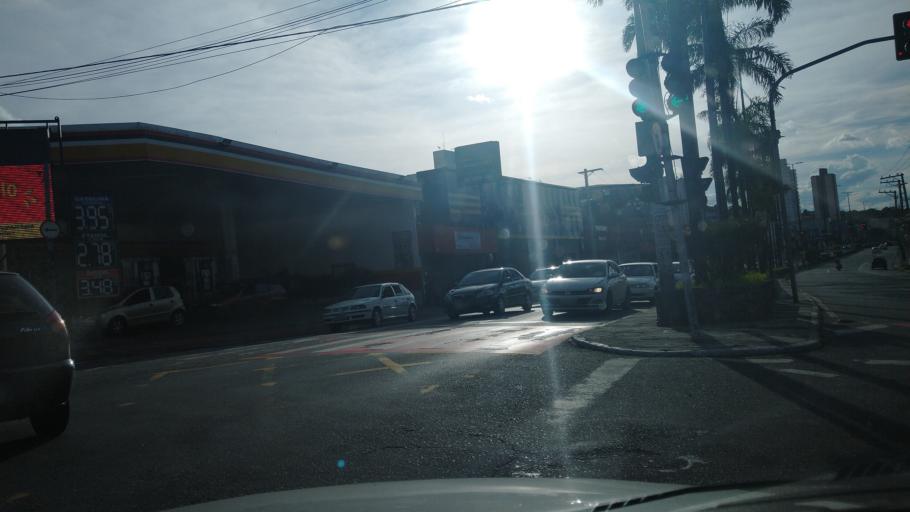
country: BR
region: Sao Paulo
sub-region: Osasco
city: Osasco
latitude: -23.5268
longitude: -46.7944
